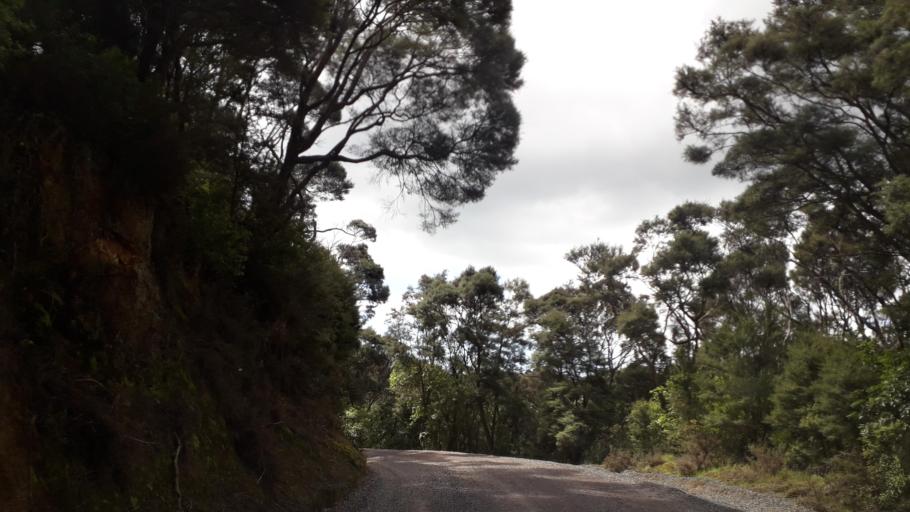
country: NZ
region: Northland
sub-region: Far North District
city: Paihia
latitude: -35.3108
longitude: 174.2236
